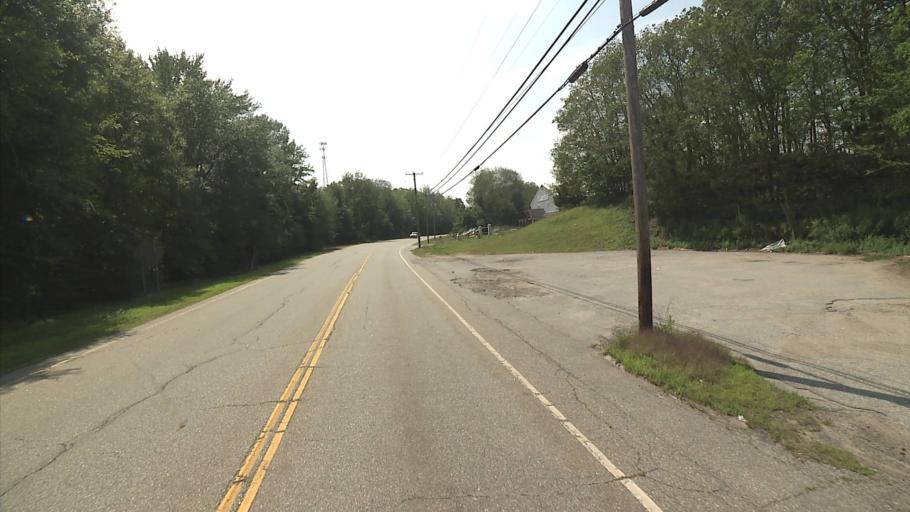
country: US
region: Connecticut
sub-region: New London County
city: Montville Center
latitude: 41.4712
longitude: -72.2710
